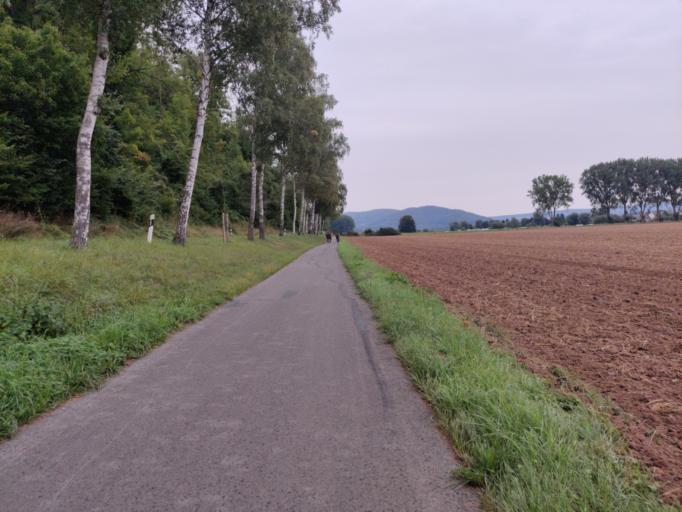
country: DE
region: Lower Saxony
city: Heinsen
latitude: 51.8890
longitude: 9.4329
